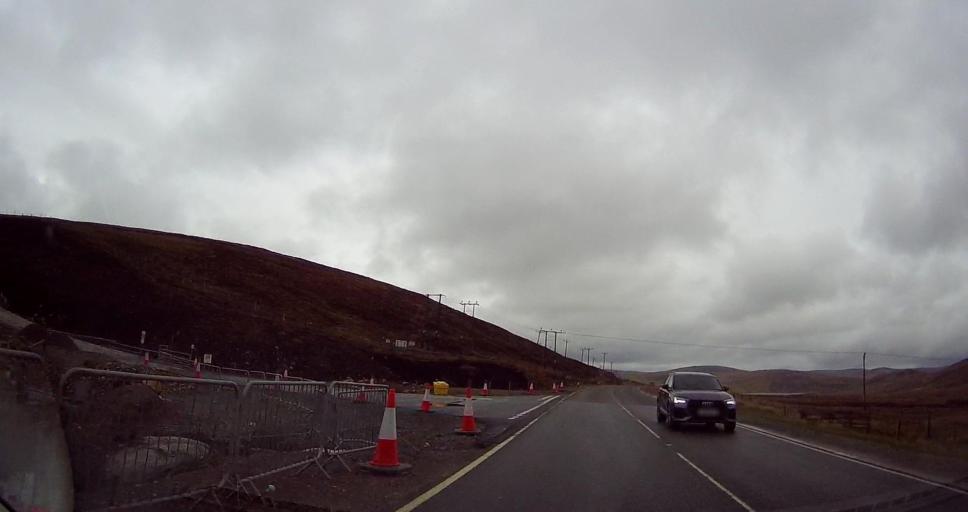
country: GB
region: Scotland
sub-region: Shetland Islands
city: Lerwick
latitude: 60.3293
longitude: -1.2538
